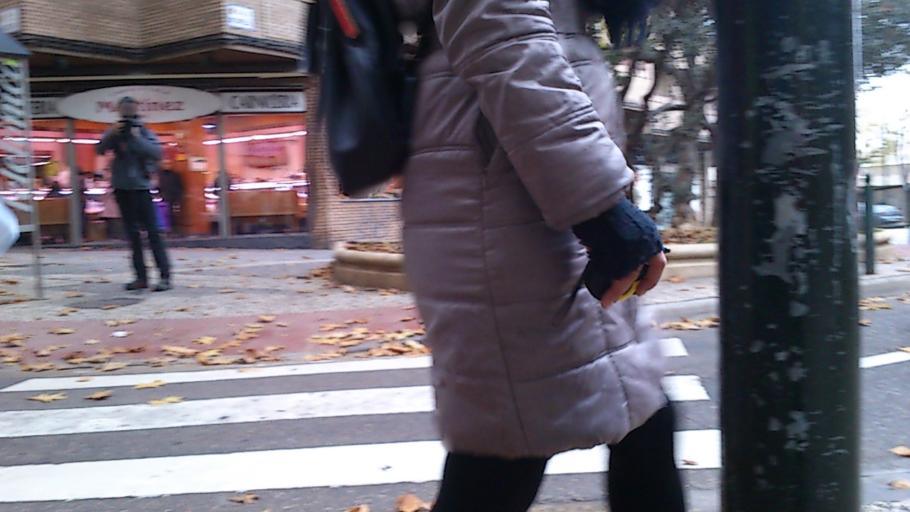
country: ES
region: Aragon
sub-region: Provincia de Zaragoza
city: Zaragoza
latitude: 41.6518
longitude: -0.8700
